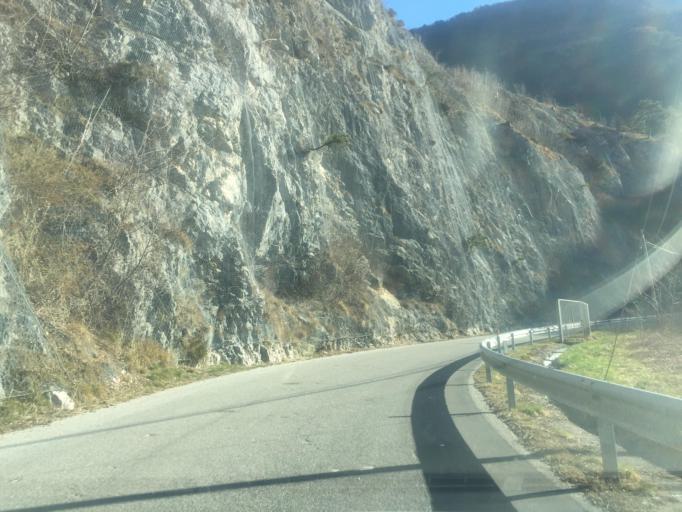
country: IT
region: Friuli Venezia Giulia
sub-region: Provincia di Udine
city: Tolmezzo
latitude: 46.4155
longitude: 13.0487
